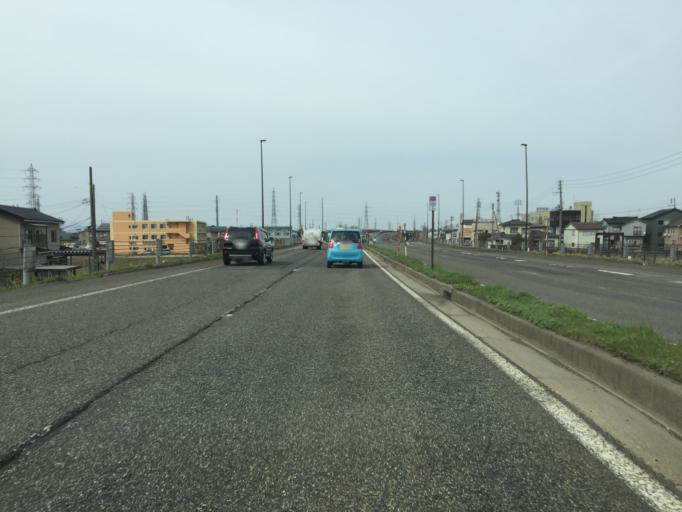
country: JP
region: Niigata
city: Nagaoka
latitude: 37.4371
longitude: 138.8676
